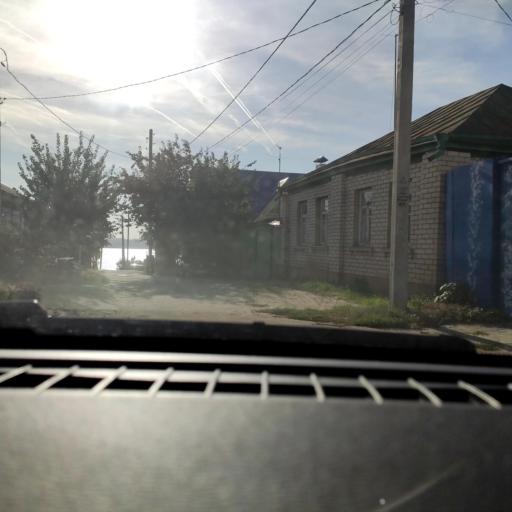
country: RU
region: Voronezj
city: Voronezh
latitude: 51.6278
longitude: 39.1980
